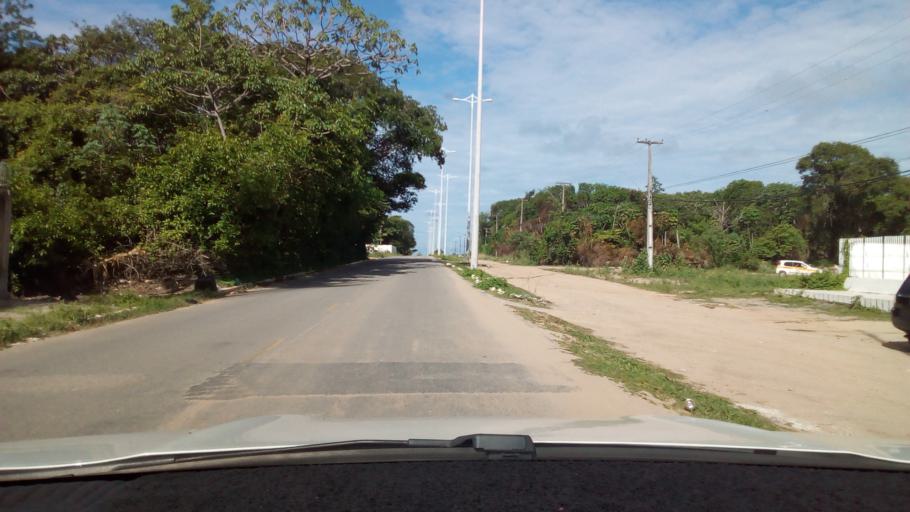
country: BR
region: Paraiba
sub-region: Joao Pessoa
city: Joao Pessoa
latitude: -7.1354
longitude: -34.8267
